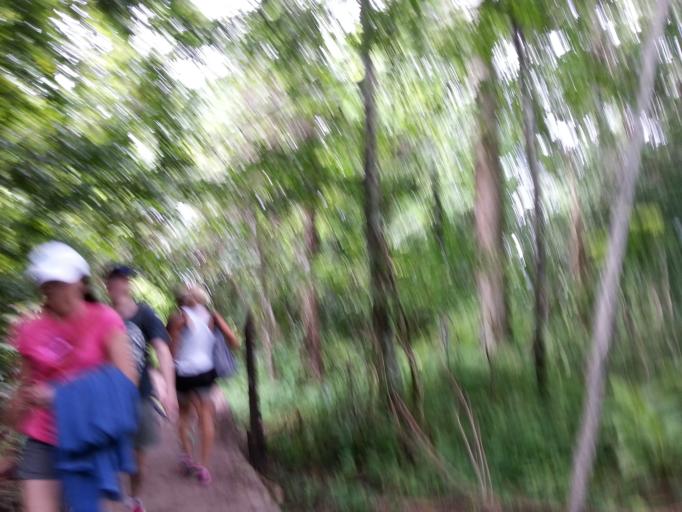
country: TH
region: Krabi
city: Khlong Thom
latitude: 7.9276
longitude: 99.2718
